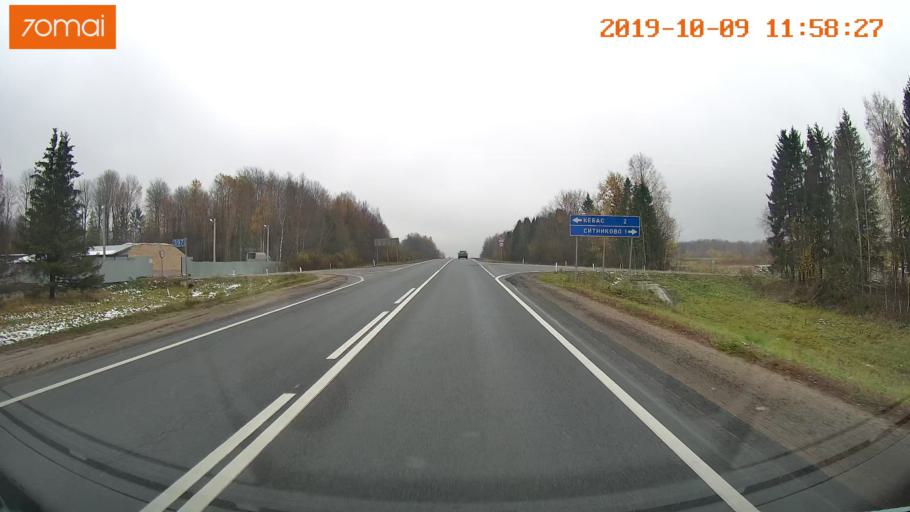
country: RU
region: Vologda
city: Gryazovets
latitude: 58.7180
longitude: 40.2965
